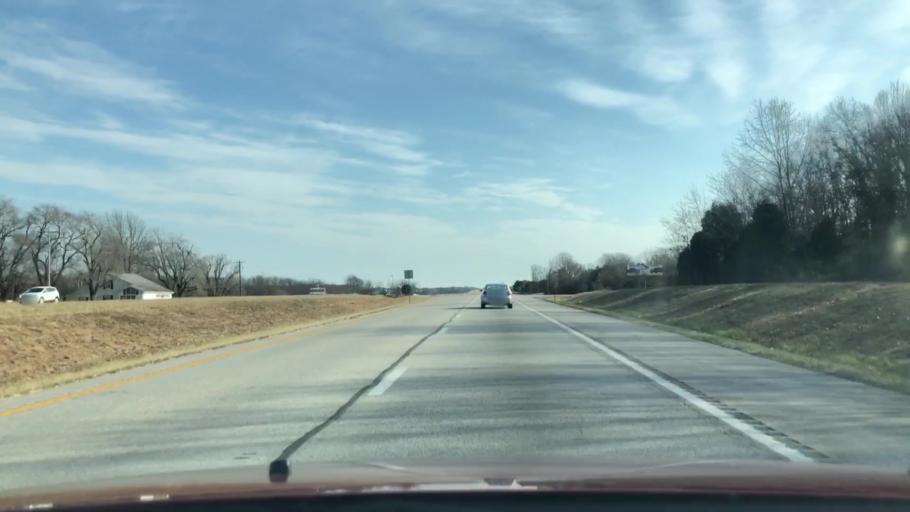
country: US
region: Missouri
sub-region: Christian County
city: Ozark
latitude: 37.1196
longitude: -93.1662
